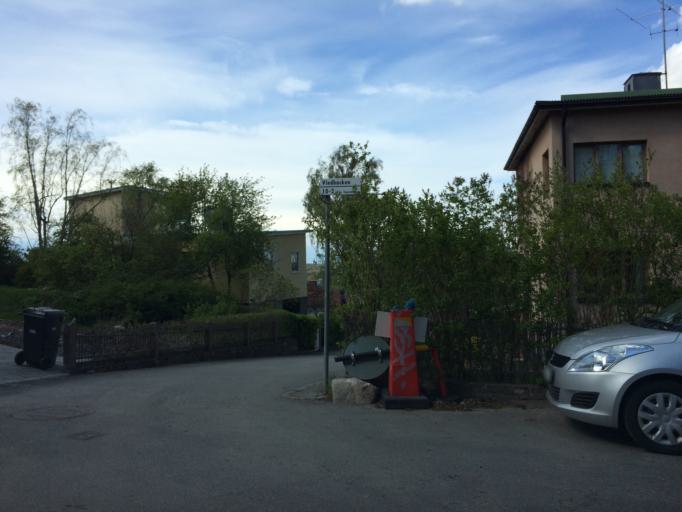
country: SE
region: Stockholm
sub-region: Huddinge Kommun
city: Segeltorp
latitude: 59.3021
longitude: 17.9511
